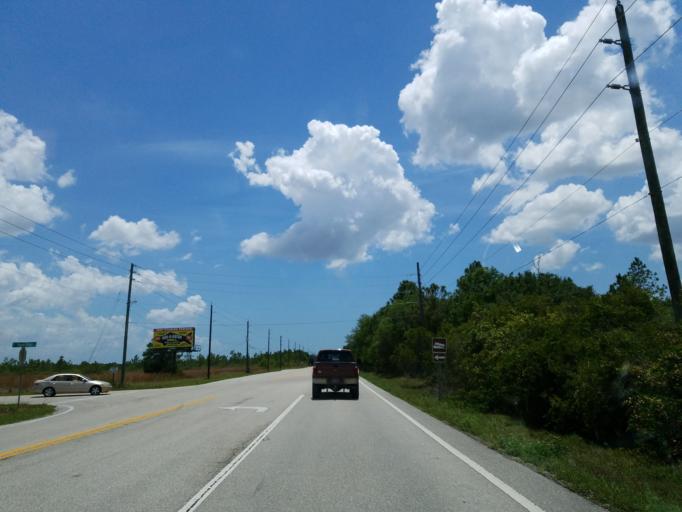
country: US
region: Florida
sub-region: Charlotte County
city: Harbour Heights
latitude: 27.0616
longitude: -82.0255
